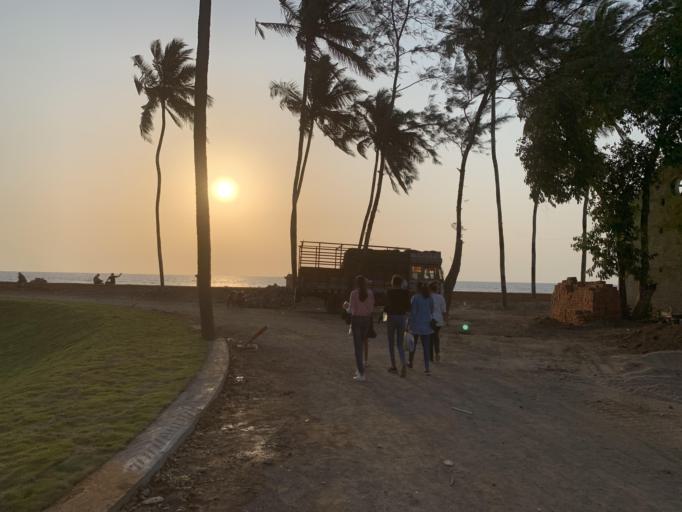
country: IN
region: Daman and Diu
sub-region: Daman District
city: Daman
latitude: 20.4468
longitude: 72.8339
